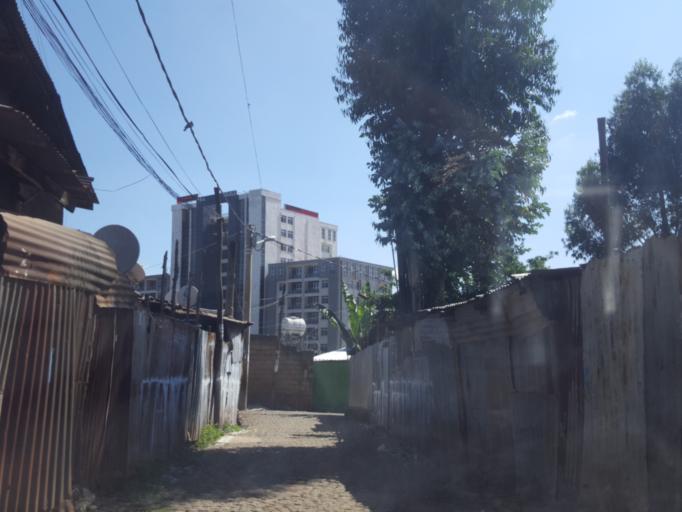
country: ET
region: Adis Abeba
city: Addis Ababa
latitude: 9.0593
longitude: 38.7340
